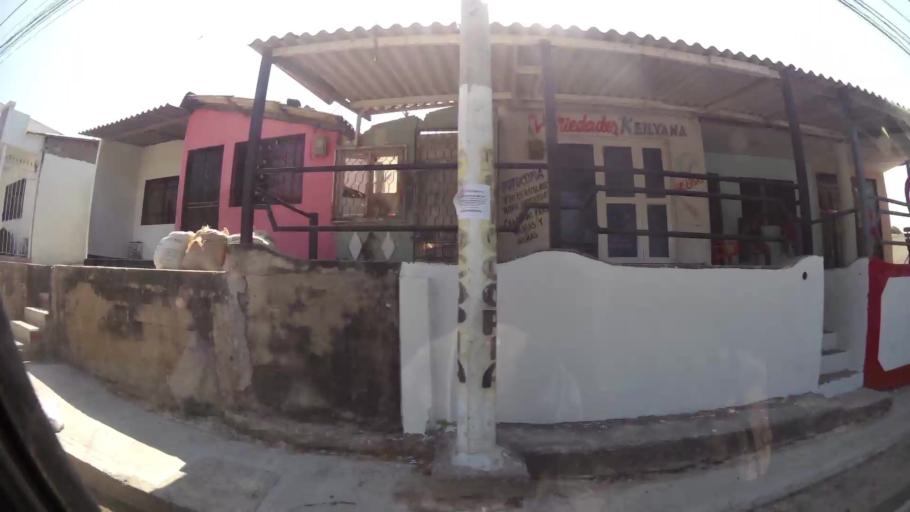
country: CO
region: Atlantico
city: Barranquilla
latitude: 10.9709
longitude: -74.8275
